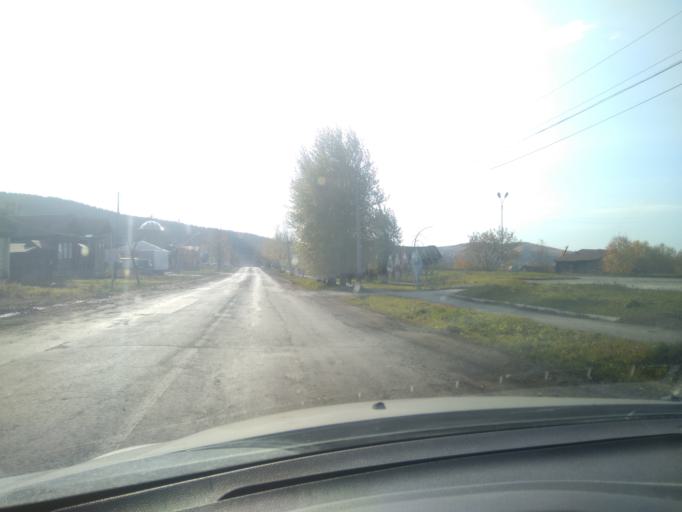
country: RU
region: Sverdlovsk
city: Nizhniye Sergi
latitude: 56.6618
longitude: 59.2995
